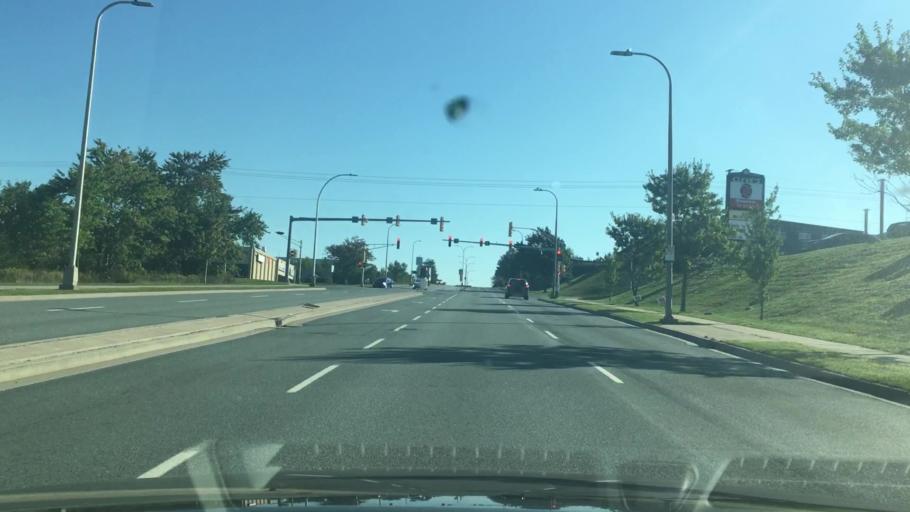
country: CA
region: Nova Scotia
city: Dartmouth
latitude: 44.7111
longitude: -63.6011
